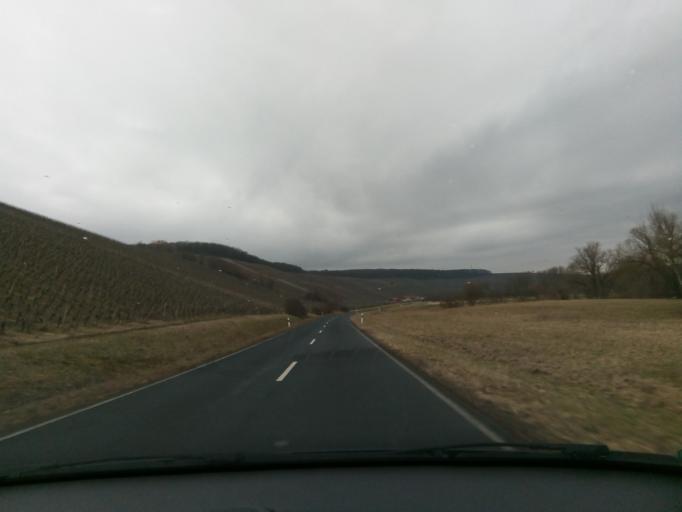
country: DE
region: Bavaria
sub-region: Regierungsbezirk Unterfranken
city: Nordheim
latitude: 49.8374
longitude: 10.1753
